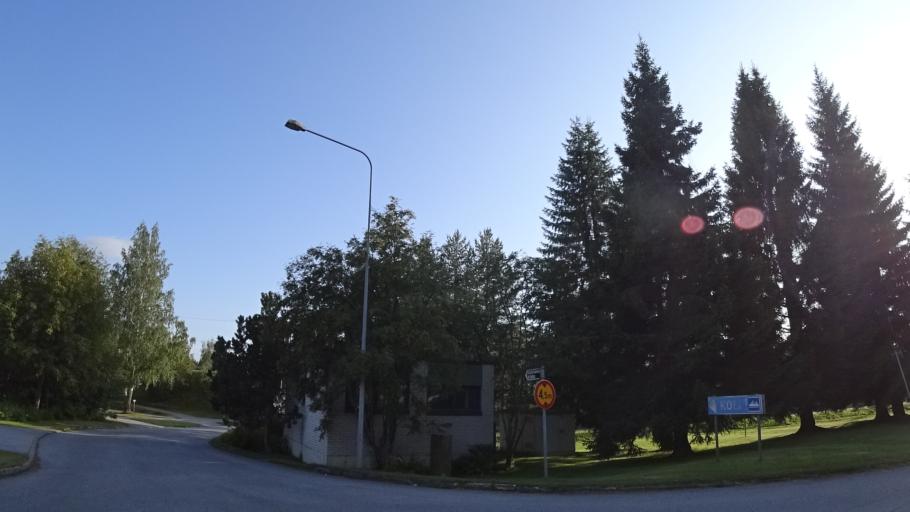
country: FI
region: North Karelia
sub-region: Pielisen Karjala
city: Lieksa
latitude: 63.3147
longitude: 30.0324
